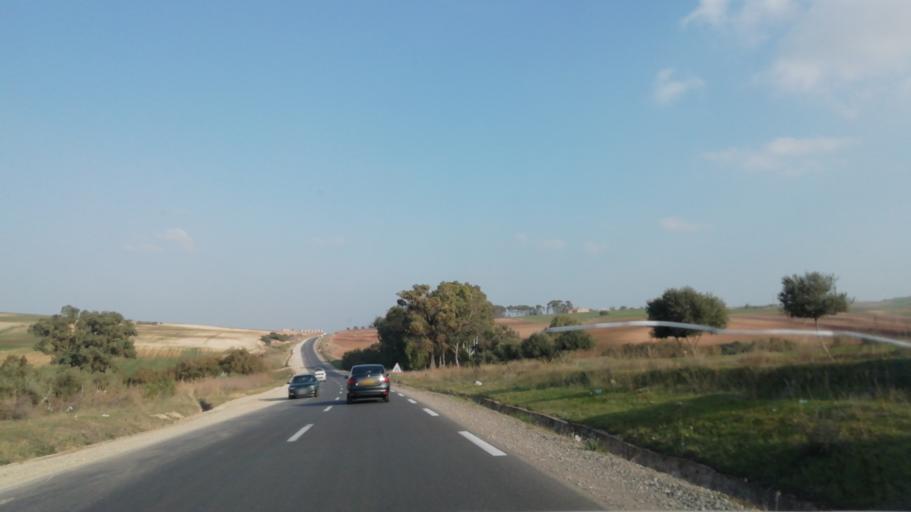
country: DZ
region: Ain Temouchent
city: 'Ain Temouchent
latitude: 35.3026
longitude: -1.0712
